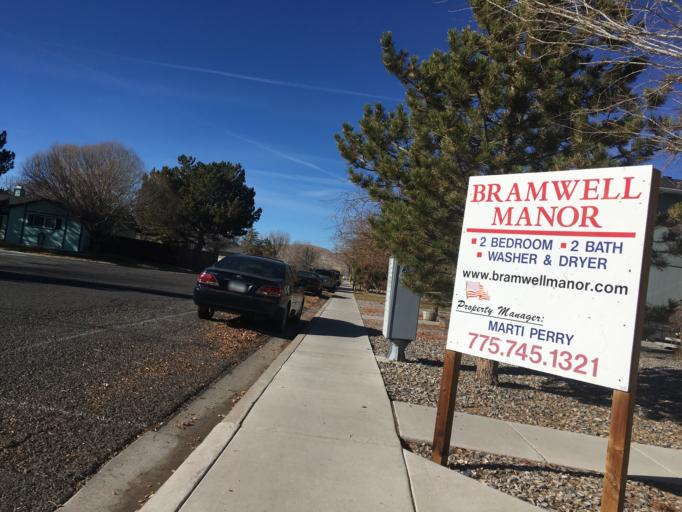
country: US
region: Nevada
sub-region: Lyon County
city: Fernley
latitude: 39.6050
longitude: -119.2424
